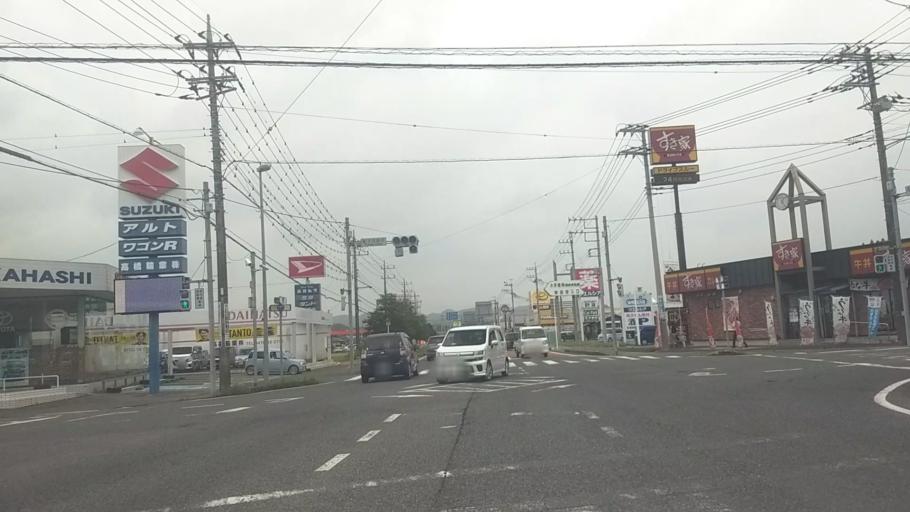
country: JP
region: Chiba
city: Ohara
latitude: 35.2858
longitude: 140.2525
